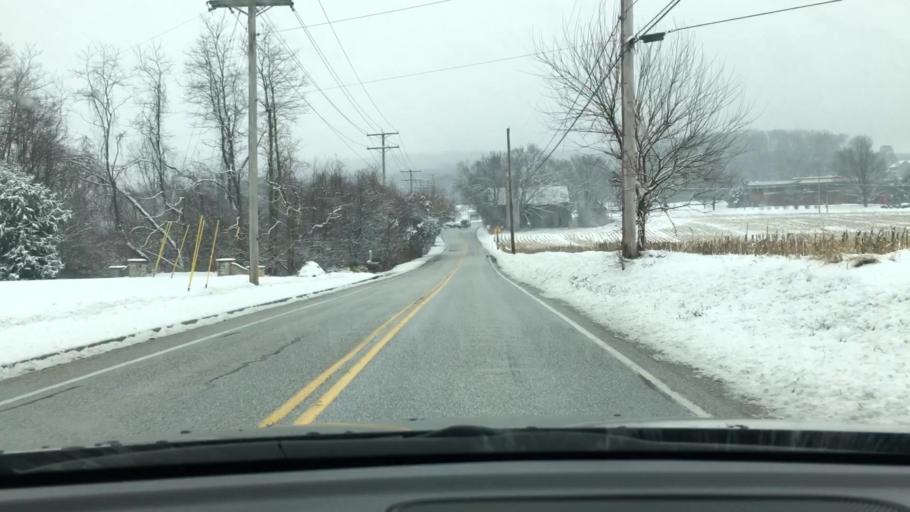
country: US
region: Pennsylvania
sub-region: York County
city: Spry
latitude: 39.9330
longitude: -76.6634
